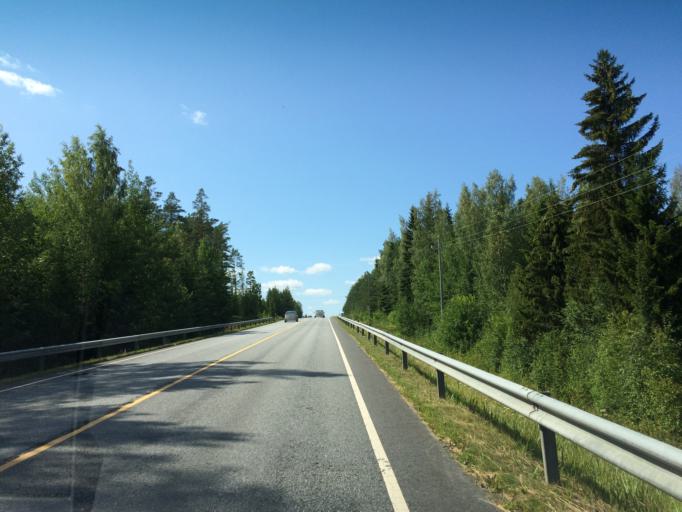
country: FI
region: Pirkanmaa
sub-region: Lounais-Pirkanmaa
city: Kiikoinen
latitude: 61.4800
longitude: 22.6026
